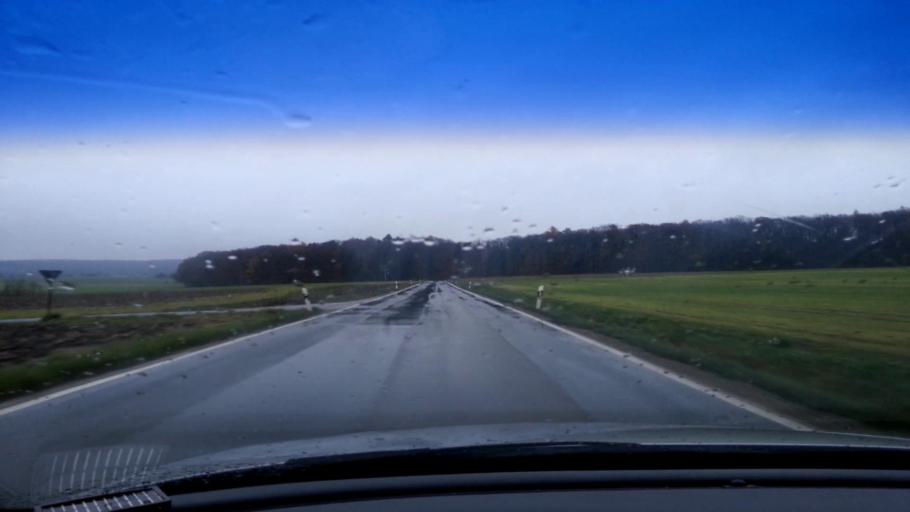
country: DE
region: Bavaria
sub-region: Upper Franconia
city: Litzendorf
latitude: 49.9420
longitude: 11.0177
